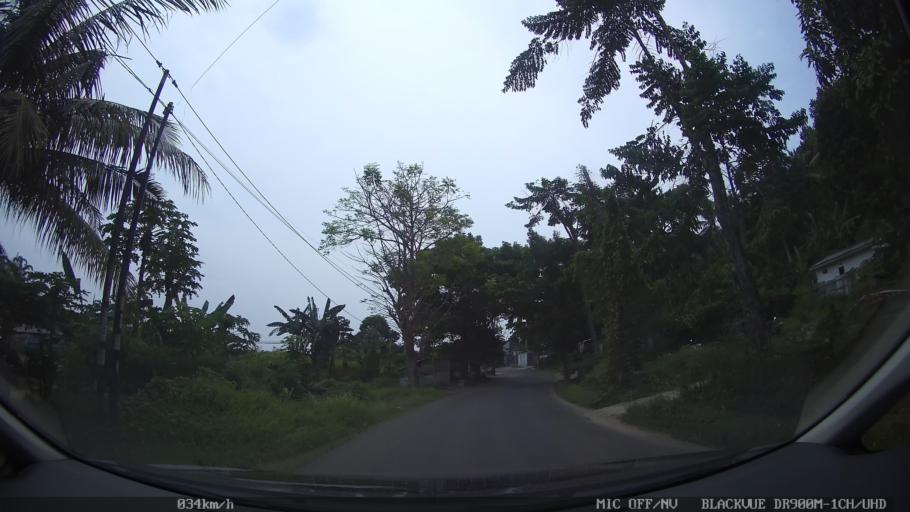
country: ID
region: Lampung
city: Bandarlampung
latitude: -5.4283
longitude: 105.2785
